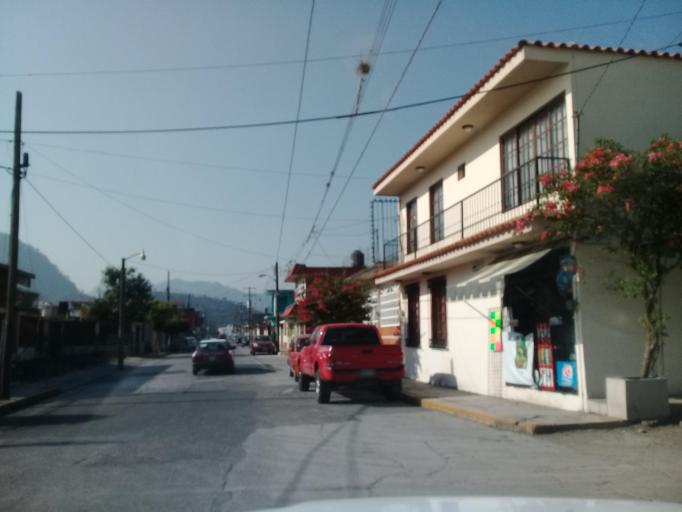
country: MX
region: Veracruz
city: Ixtac Zoquitlan
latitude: 18.8569
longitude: -97.0683
